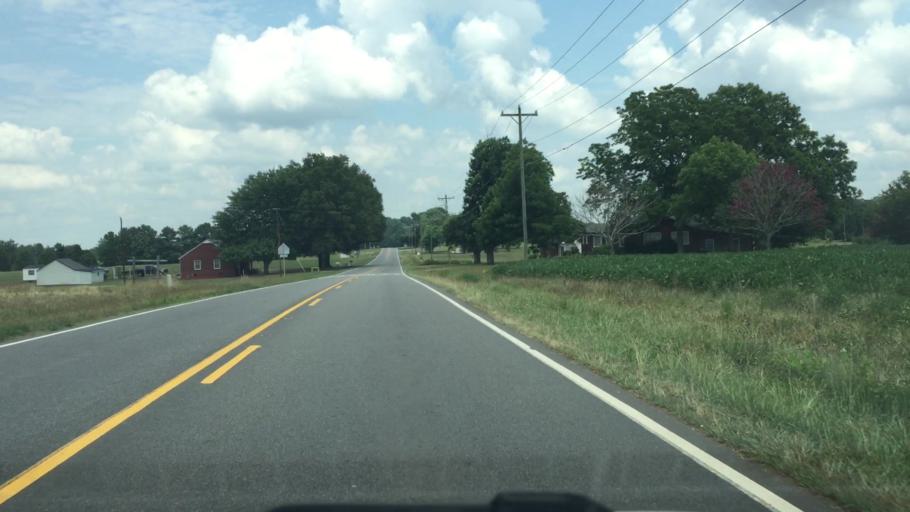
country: US
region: North Carolina
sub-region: Iredell County
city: Troutman
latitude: 35.7178
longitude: -80.8850
